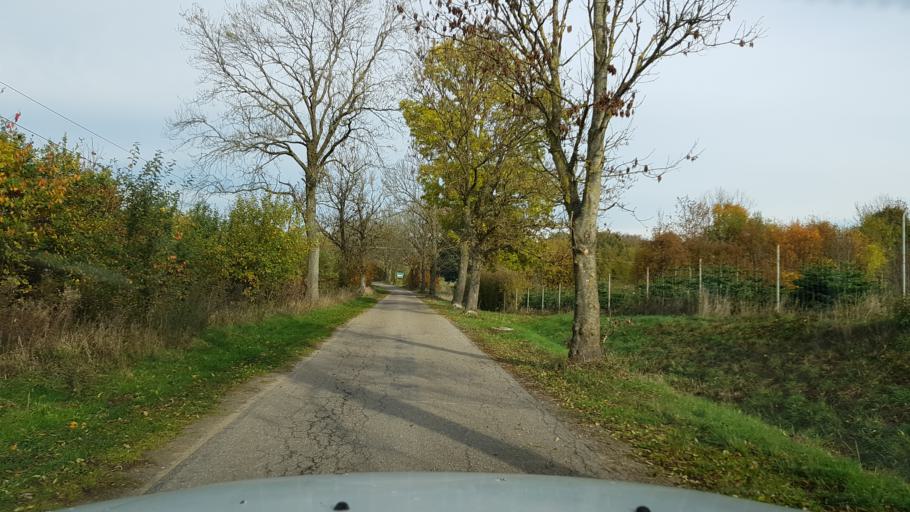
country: PL
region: West Pomeranian Voivodeship
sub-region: Powiat swidwinski
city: Polczyn-Zdroj
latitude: 53.7380
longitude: 16.0360
